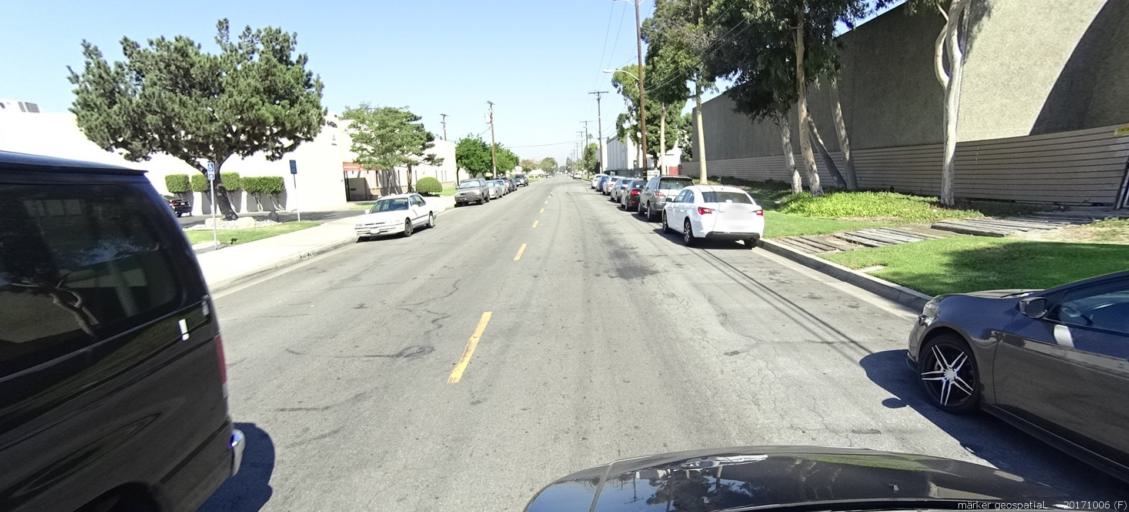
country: US
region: California
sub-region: Orange County
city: Westminster
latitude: 33.7776
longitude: -118.0057
